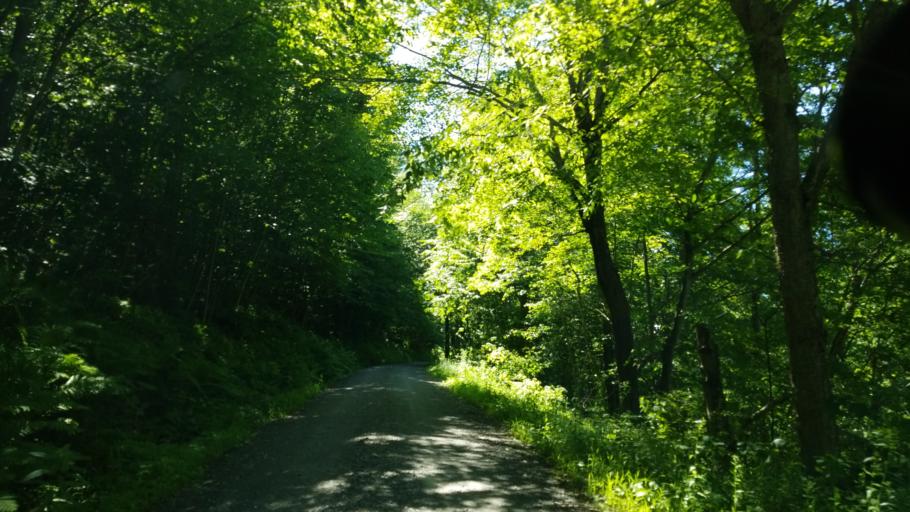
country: US
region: Pennsylvania
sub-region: Clearfield County
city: Shiloh
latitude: 41.2180
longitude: -78.3816
